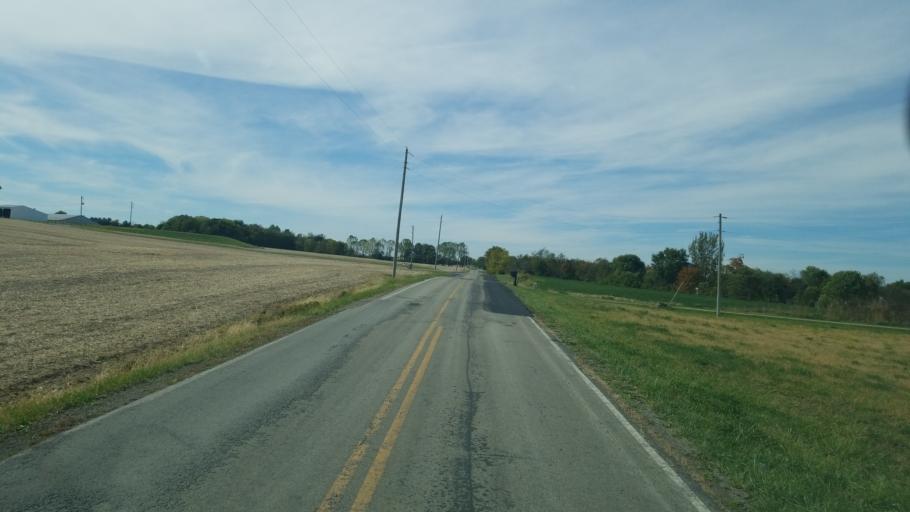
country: US
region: Ohio
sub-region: Highland County
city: Leesburg
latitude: 39.3285
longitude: -83.4866
